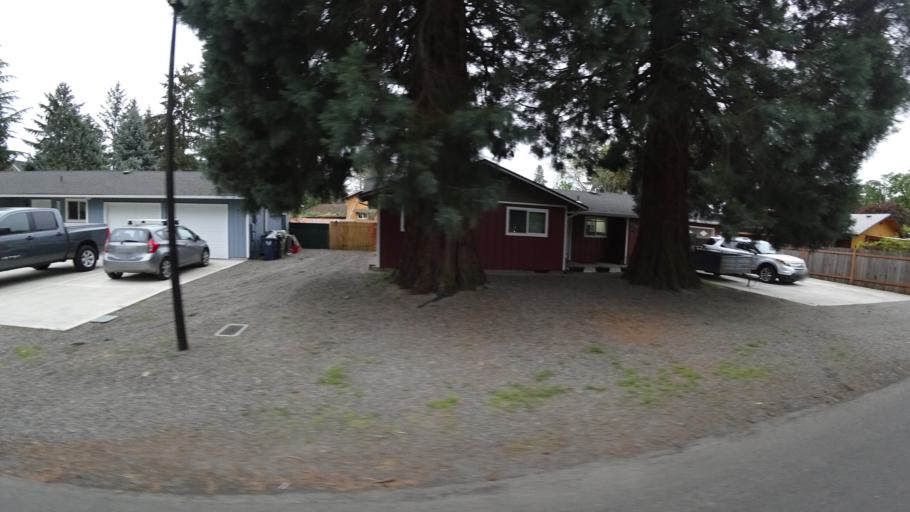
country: US
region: Oregon
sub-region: Washington County
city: Aloha
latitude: 45.5079
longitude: -122.8827
